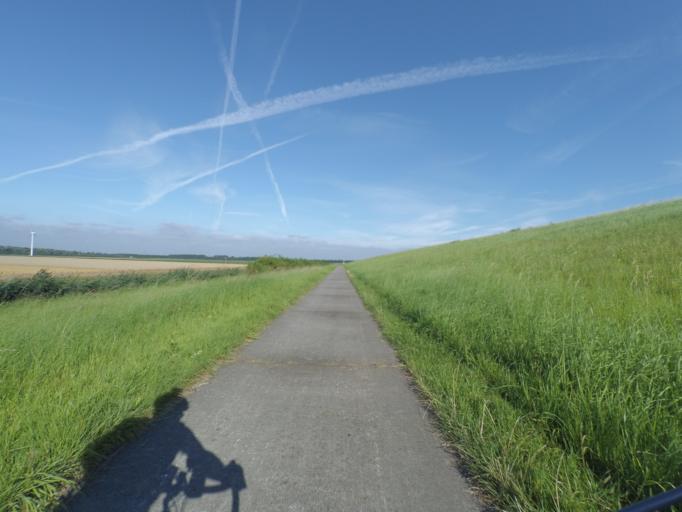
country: NL
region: Flevoland
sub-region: Gemeente Lelystad
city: Lelystad
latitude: 52.4350
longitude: 5.4501
